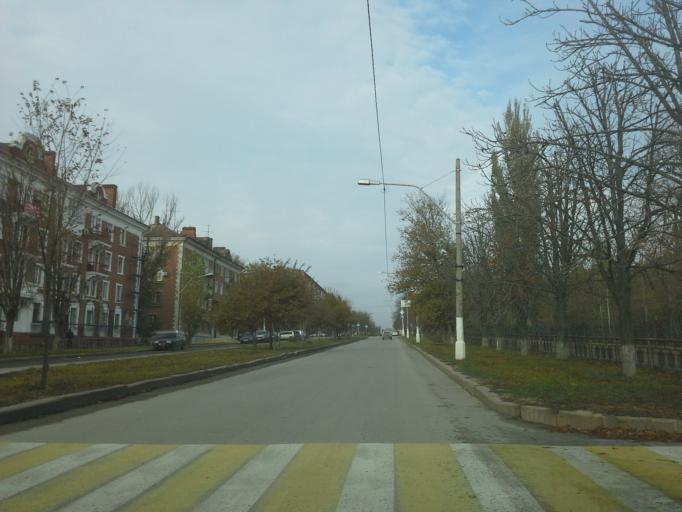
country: RU
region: Volgograd
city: Vodstroy
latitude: 48.7797
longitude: 44.5716
